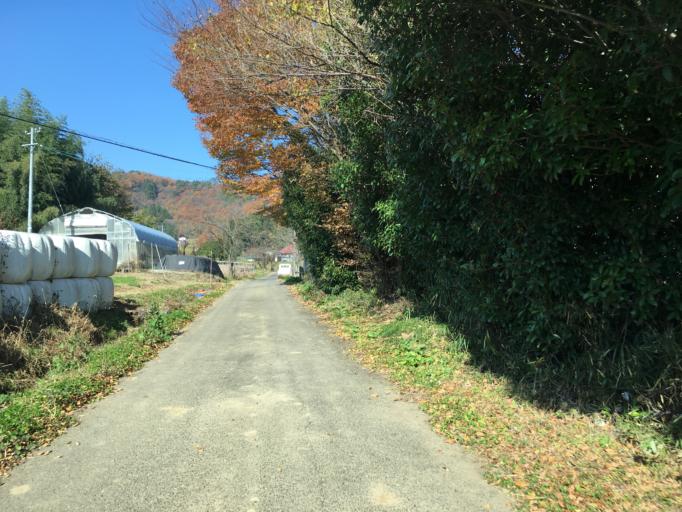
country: JP
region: Fukushima
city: Nihommatsu
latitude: 37.5726
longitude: 140.3774
